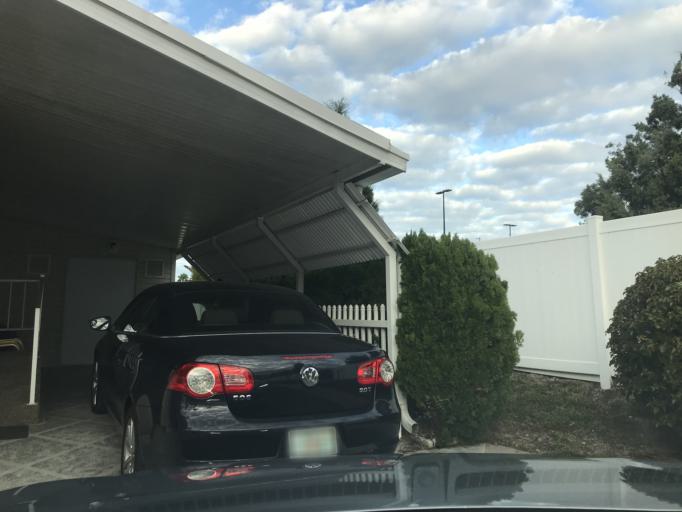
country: US
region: Florida
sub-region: Pinellas County
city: Largo
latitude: 27.9256
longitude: -82.7860
